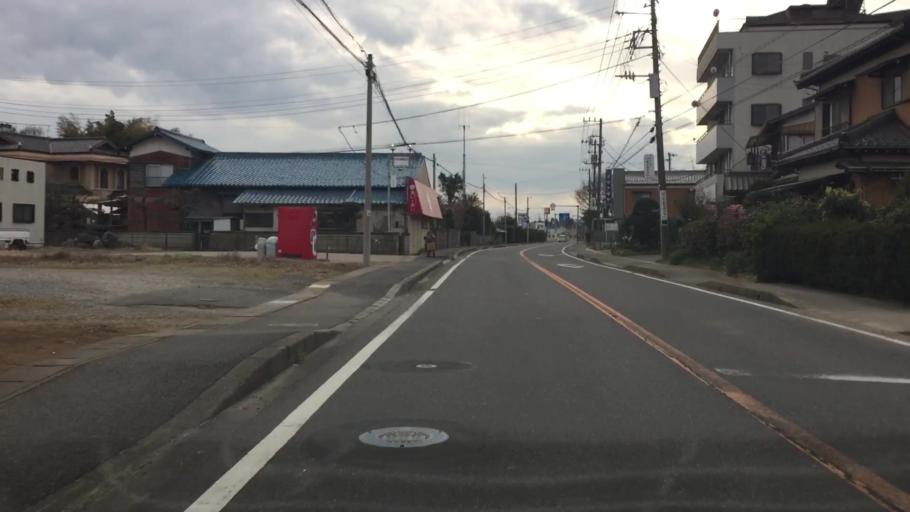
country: JP
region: Chiba
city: Shiroi
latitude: 35.7868
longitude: 140.0499
